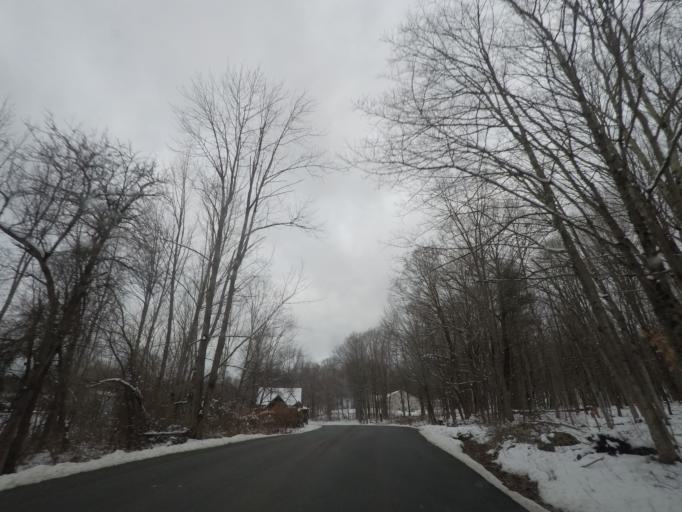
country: US
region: New York
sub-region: Rensselaer County
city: Averill Park
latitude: 42.6517
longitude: -73.5349
